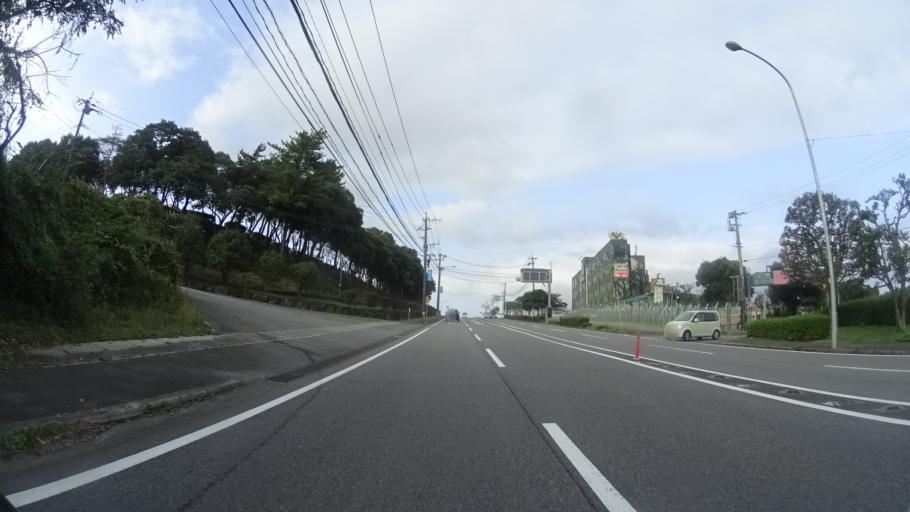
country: JP
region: Oita
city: Beppu
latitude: 33.2938
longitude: 131.4603
